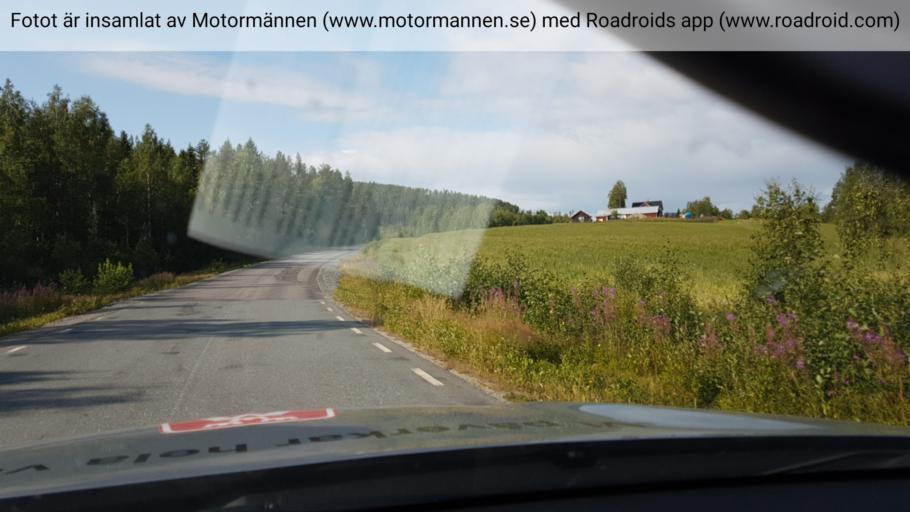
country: SE
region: Norrbotten
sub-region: Alvsbyns Kommun
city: AElvsbyn
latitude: 65.6657
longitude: 20.8873
